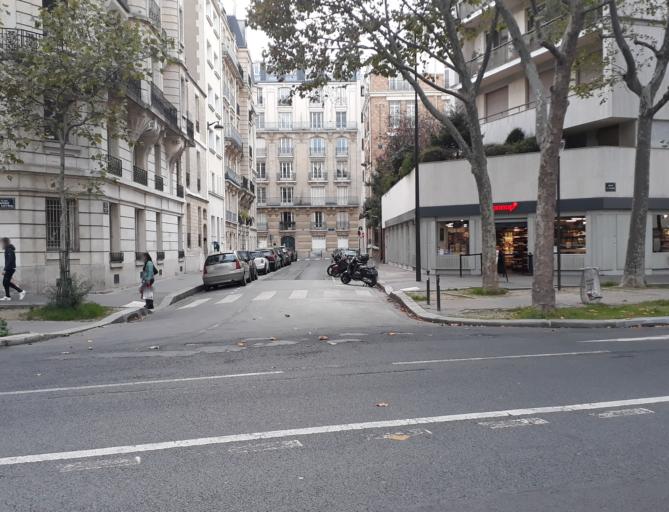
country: FR
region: Ile-de-France
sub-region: Departement des Hauts-de-Seine
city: Malakoff
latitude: 48.8481
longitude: 2.3059
